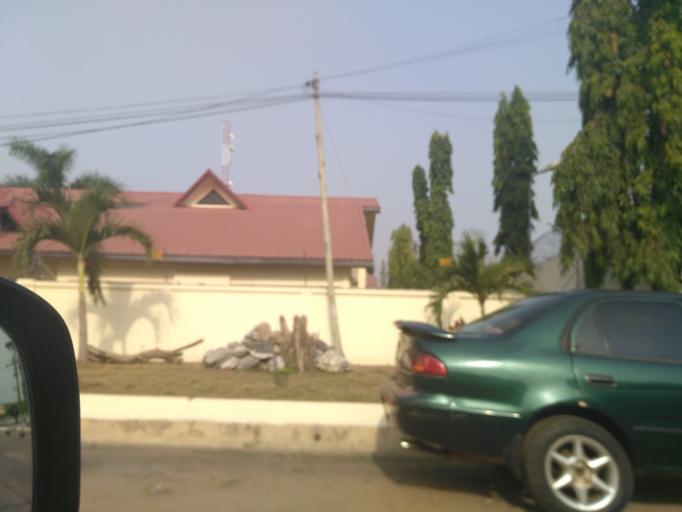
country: GH
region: Greater Accra
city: Accra
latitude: 5.6066
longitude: -0.2003
